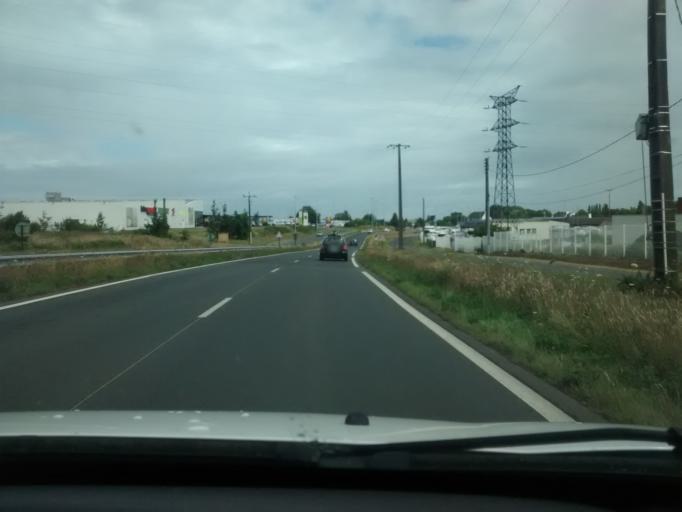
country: FR
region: Brittany
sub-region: Departement des Cotes-d'Armor
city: Saint-Quay-Perros
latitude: 48.7839
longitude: -3.4488
